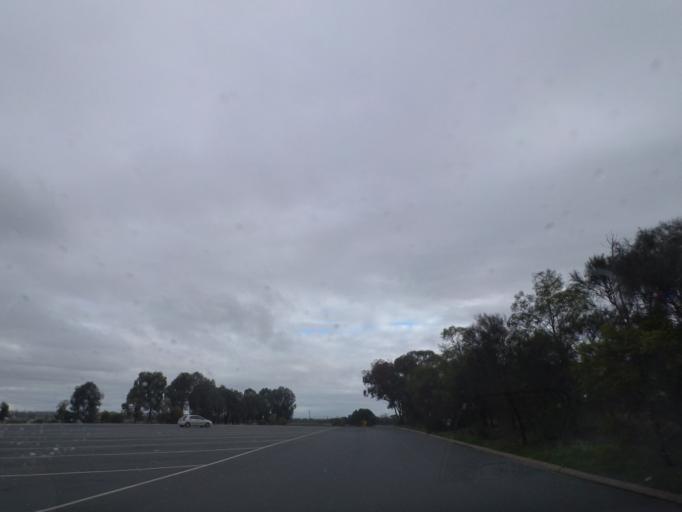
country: AU
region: Victoria
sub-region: Wangaratta
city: Wangaratta
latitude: -36.2220
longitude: 146.4458
